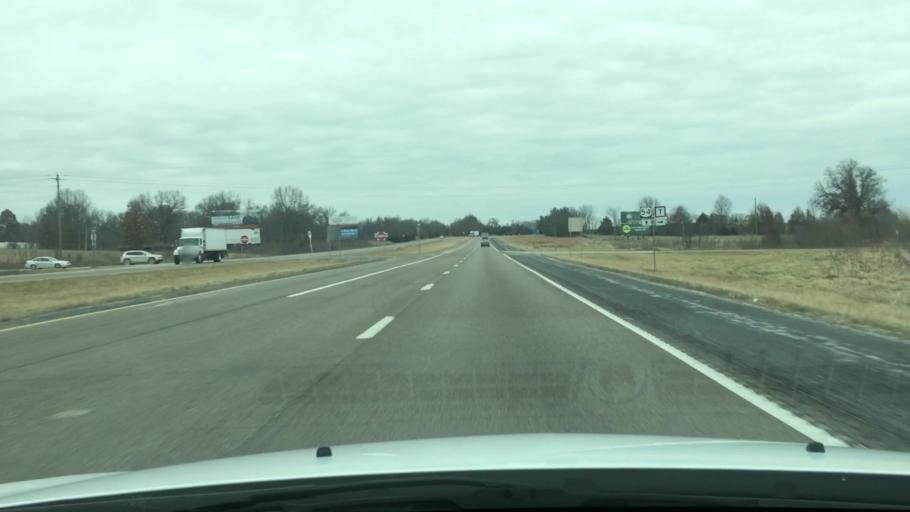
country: US
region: Missouri
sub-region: Callaway County
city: Fulton
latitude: 39.0025
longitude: -91.8934
